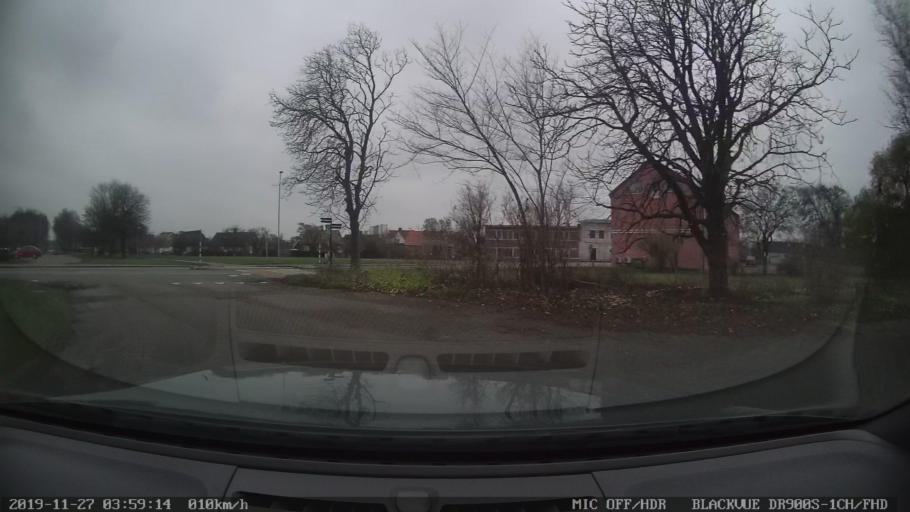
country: SE
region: Skane
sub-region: Hoganas Kommun
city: Hoganas
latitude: 56.2050
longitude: 12.5512
